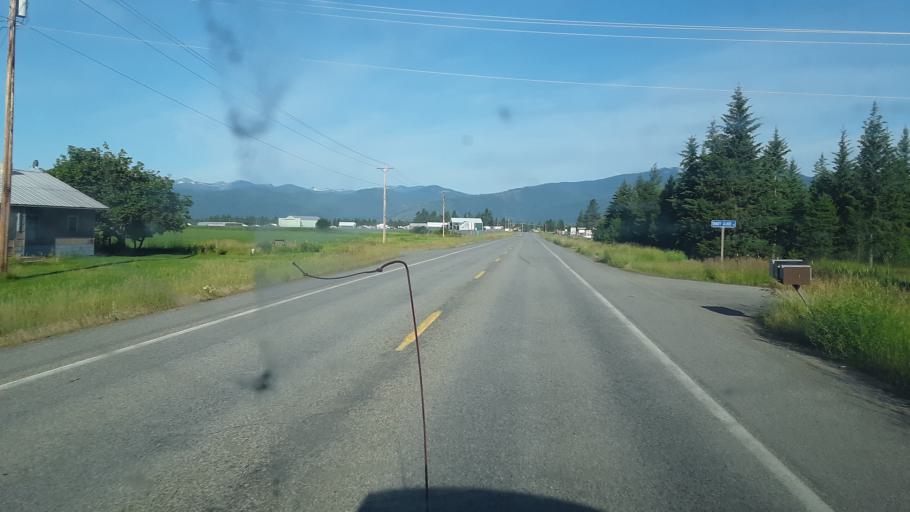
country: US
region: Idaho
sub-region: Boundary County
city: Bonners Ferry
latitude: 48.7314
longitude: -116.2839
